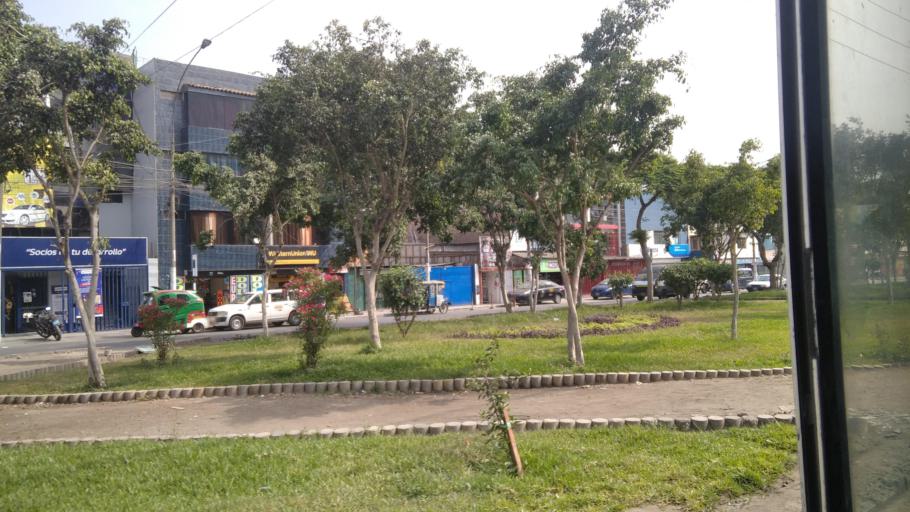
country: PE
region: Lima
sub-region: Lima
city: Independencia
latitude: -11.9705
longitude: -77.0063
